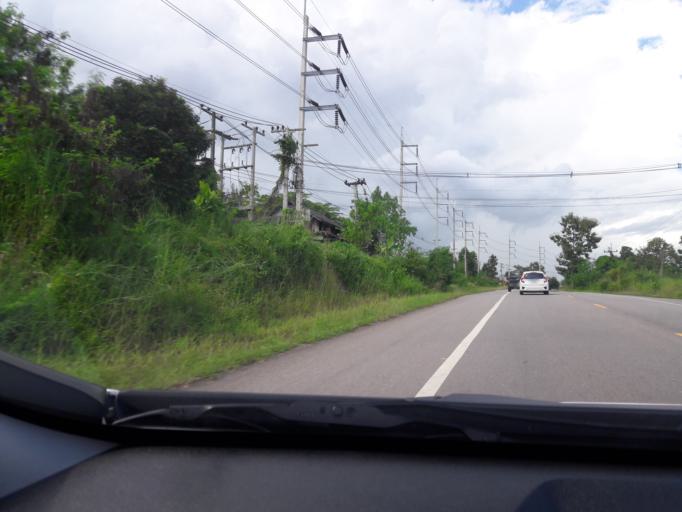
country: TH
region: Mae Hong Son
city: Mae Hi
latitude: 19.3329
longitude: 98.4327
